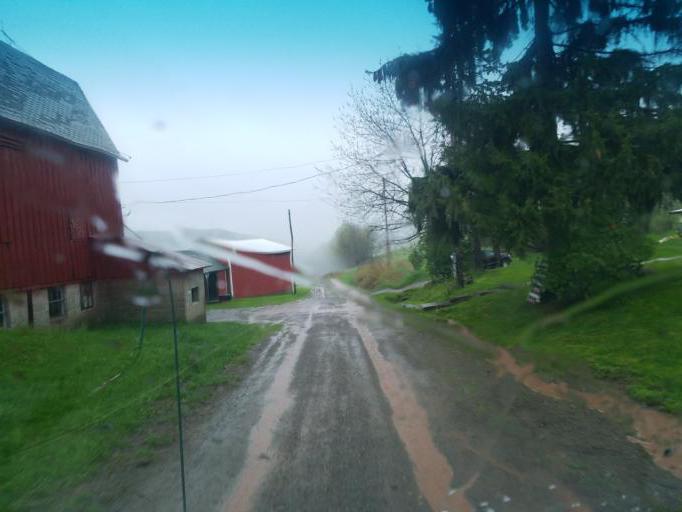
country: US
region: Pennsylvania
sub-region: Tioga County
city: Westfield
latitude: 41.9121
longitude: -77.6542
